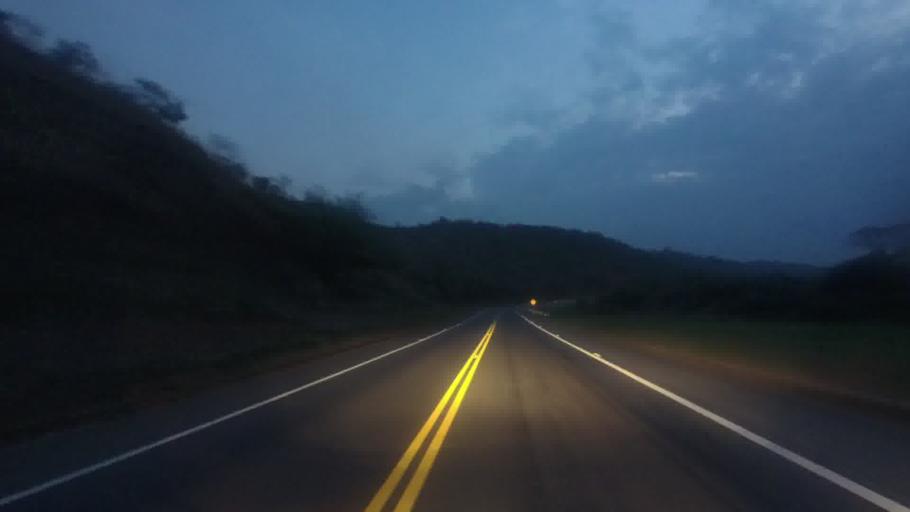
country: BR
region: Rio de Janeiro
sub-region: Sapucaia
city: Sapucaia
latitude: -21.9447
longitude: -42.8334
